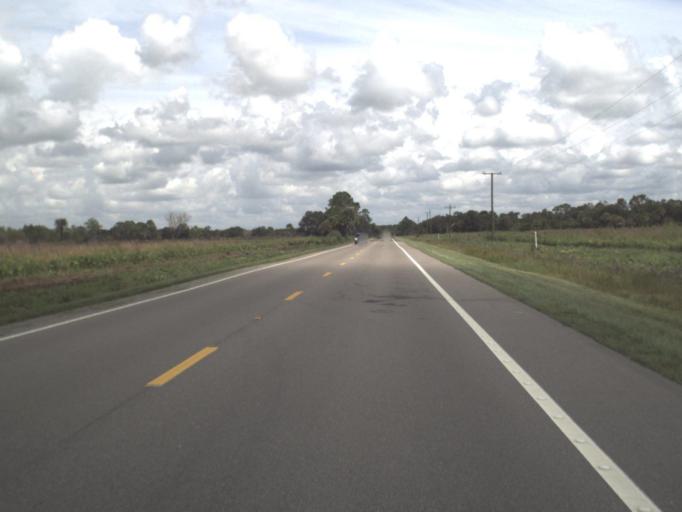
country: US
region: Florida
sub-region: Sarasota County
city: Lake Sarasota
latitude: 27.2428
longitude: -82.3355
